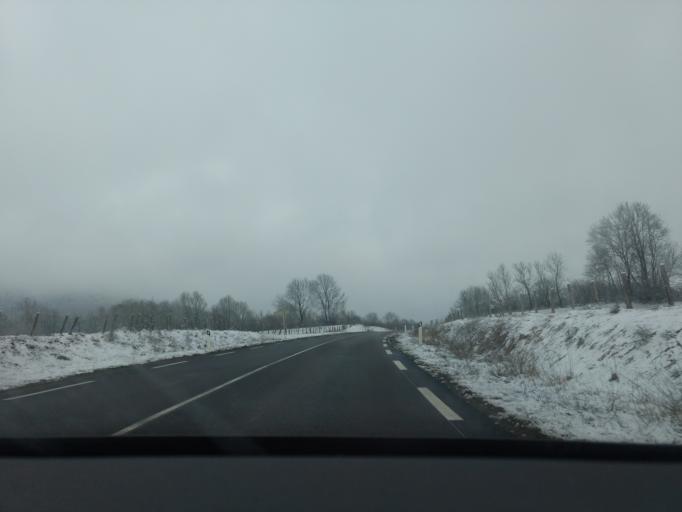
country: FR
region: Franche-Comte
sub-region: Departement du Jura
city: Champagnole
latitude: 46.7740
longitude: 5.9054
